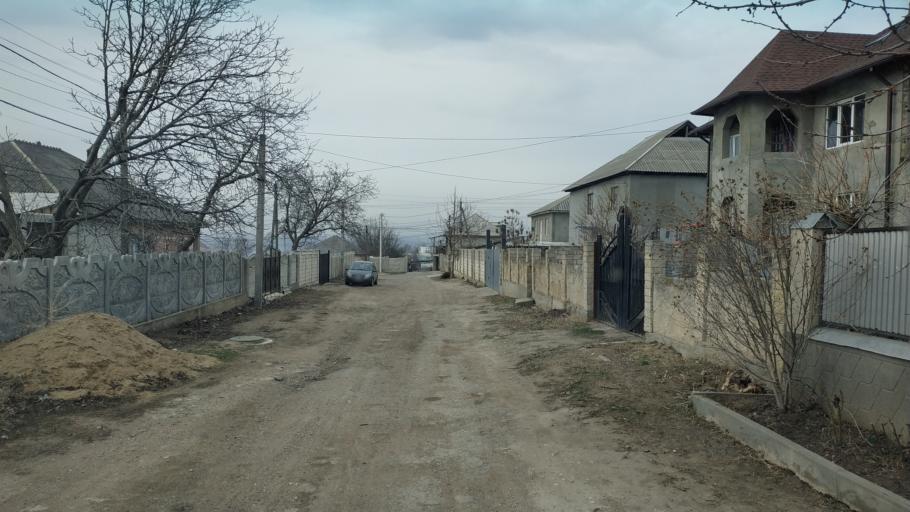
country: MD
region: Chisinau
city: Singera
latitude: 46.9373
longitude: 28.9857
